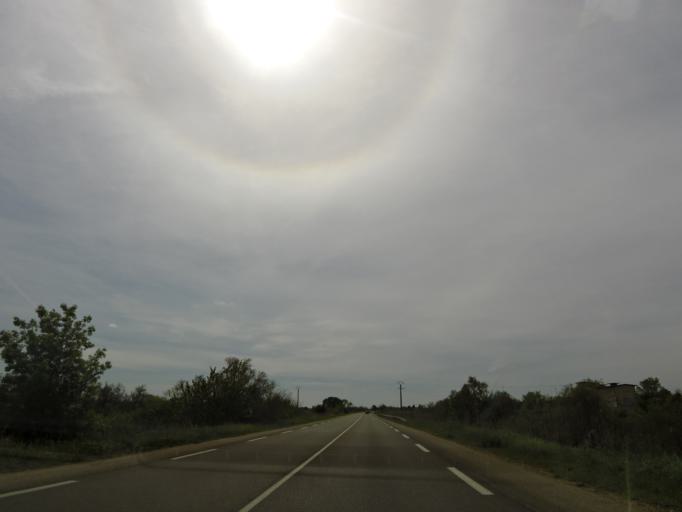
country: FR
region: Languedoc-Roussillon
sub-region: Departement de l'Herault
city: Candillargues
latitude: 43.6050
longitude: 4.1064
